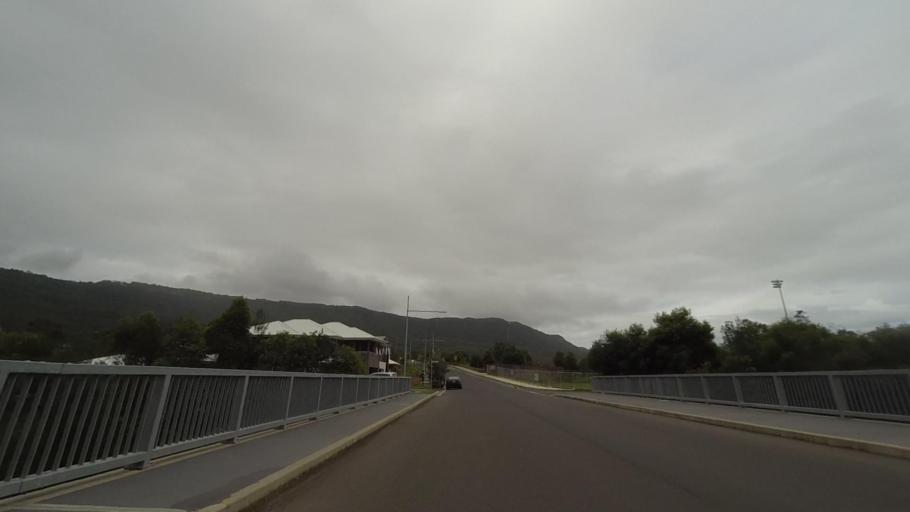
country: AU
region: New South Wales
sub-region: Wollongong
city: Bulli
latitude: -34.3213
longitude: 150.9178
